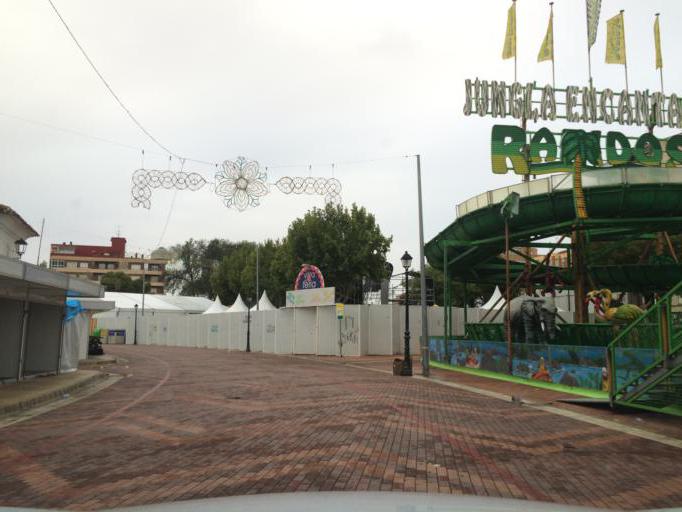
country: ES
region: Castille-La Mancha
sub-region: Provincia de Albacete
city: Albacete
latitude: 38.9979
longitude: -1.8700
